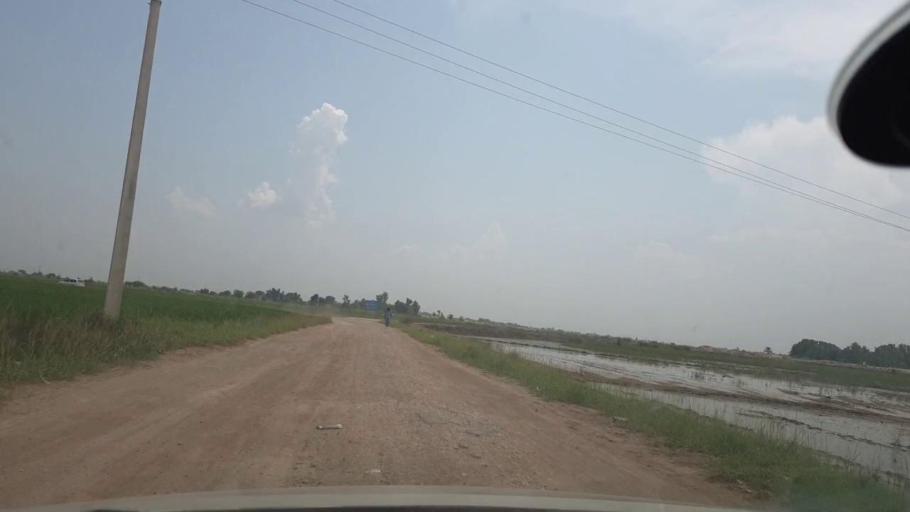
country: PK
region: Sindh
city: Jacobabad
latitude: 28.1433
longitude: 68.3546
